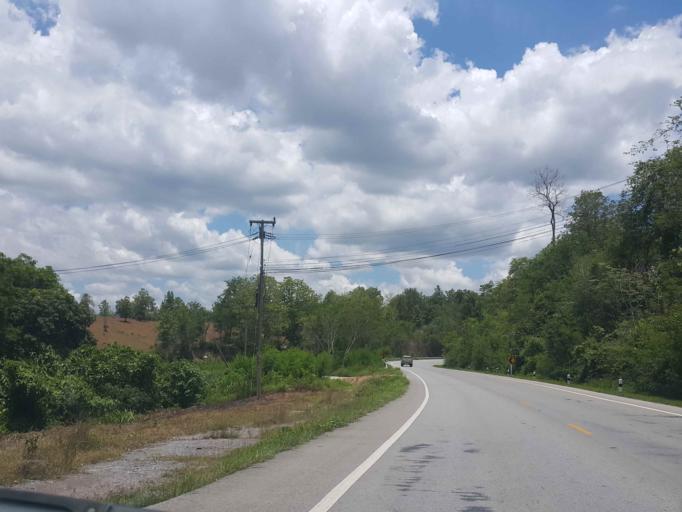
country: TH
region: Nan
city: Wiang Sa
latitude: 18.5225
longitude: 100.6103
